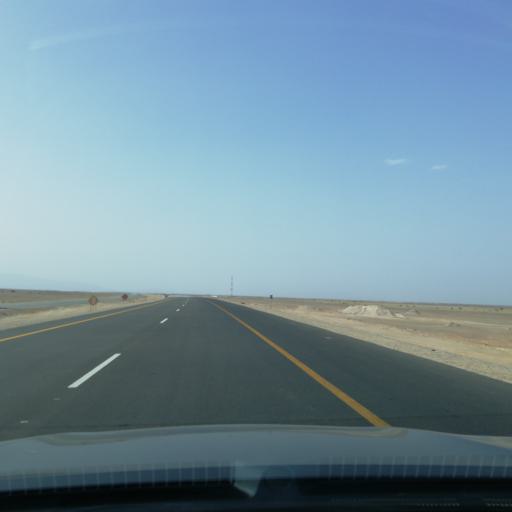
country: OM
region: Muhafazat ad Dakhiliyah
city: Adam
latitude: 22.1317
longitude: 57.5255
